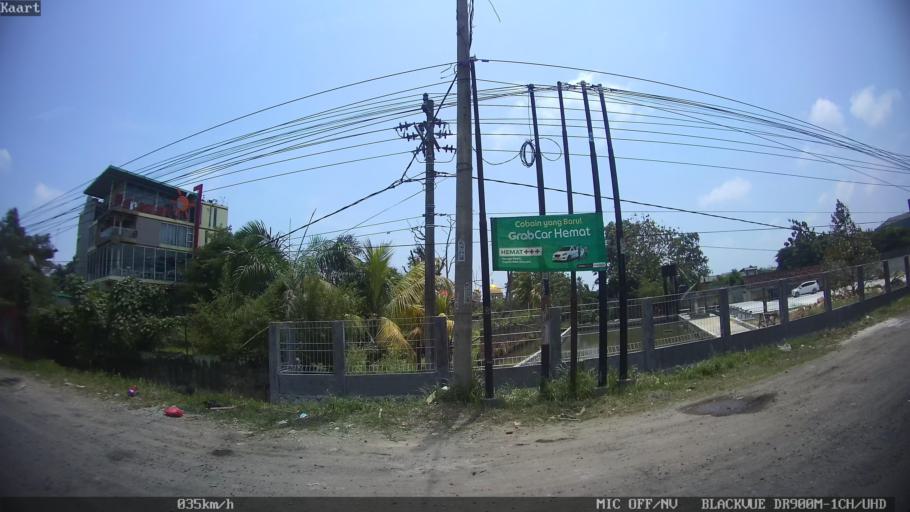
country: ID
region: Lampung
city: Kedaton
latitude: -5.3646
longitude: 105.2638
